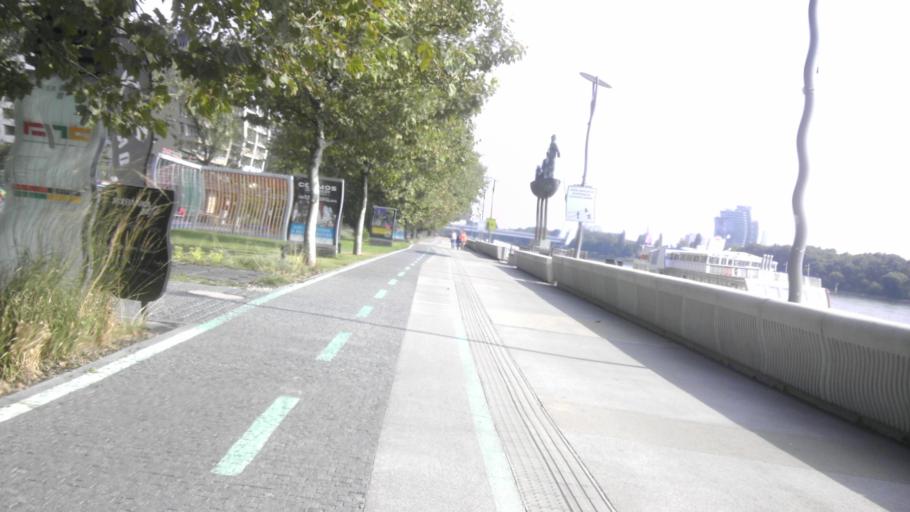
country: SK
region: Bratislavsky
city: Bratislava
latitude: 48.1409
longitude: 17.0913
